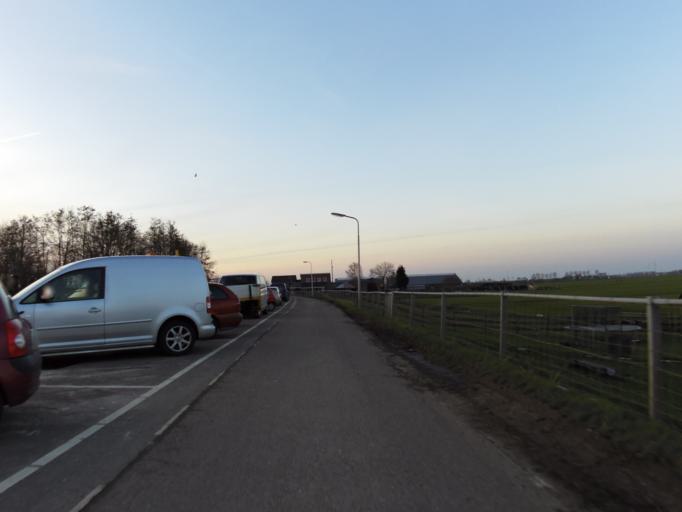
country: NL
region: South Holland
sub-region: Gemeente Kaag en Braassem
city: Oude Wetering
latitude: 52.1769
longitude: 4.5974
